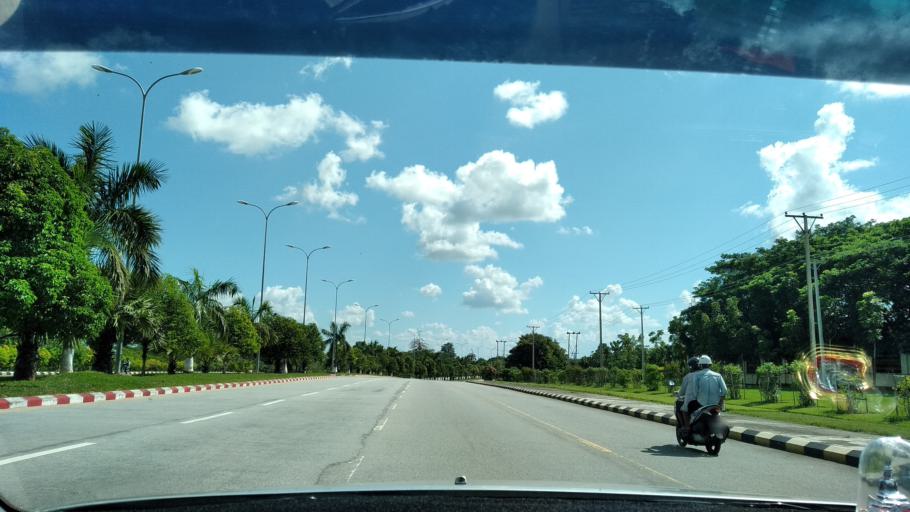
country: MM
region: Mandalay
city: Nay Pyi Taw
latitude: 19.7837
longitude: 96.1443
